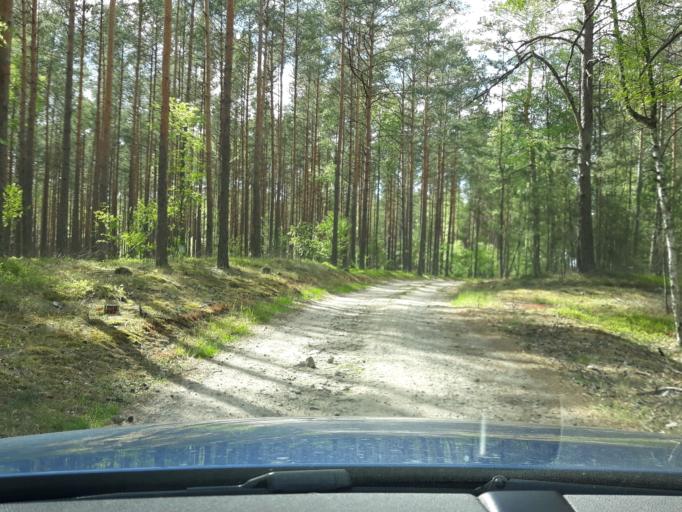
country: PL
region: Pomeranian Voivodeship
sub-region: Powiat czluchowski
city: Czluchow
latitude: 53.7193
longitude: 17.3343
